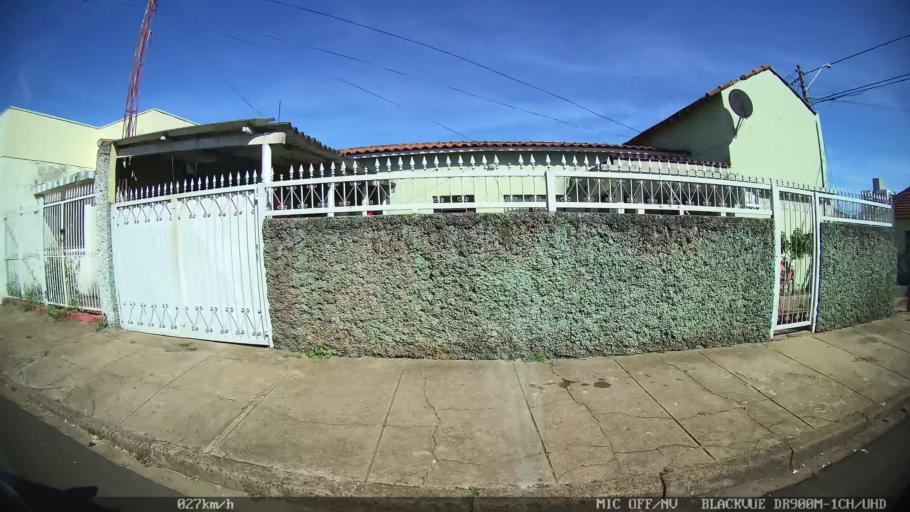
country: BR
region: Sao Paulo
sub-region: Franca
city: Franca
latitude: -20.5479
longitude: -47.3943
